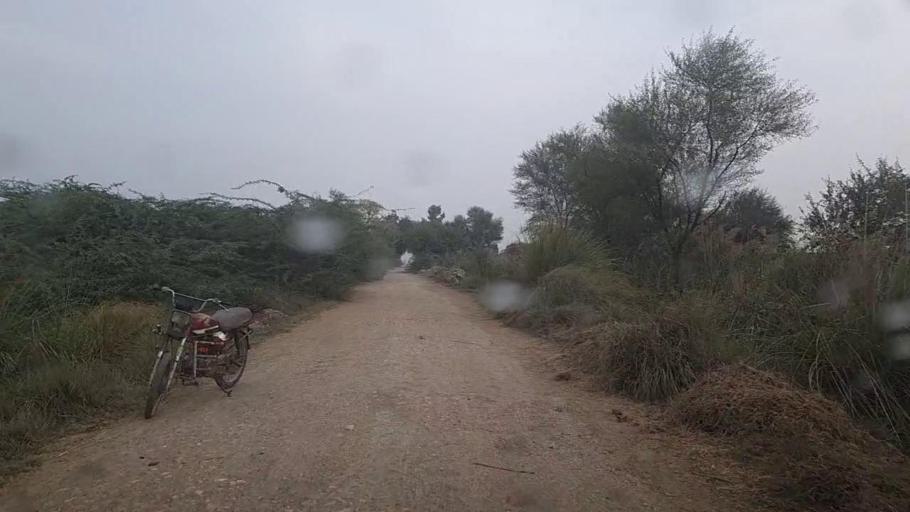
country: PK
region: Sindh
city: Gambat
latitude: 27.3729
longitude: 68.5673
